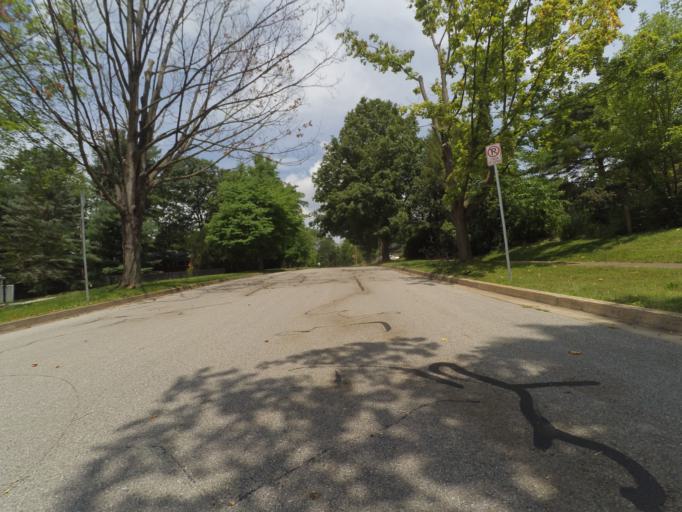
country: US
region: Pennsylvania
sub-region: Centre County
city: State College
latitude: 40.7863
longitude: -77.8423
